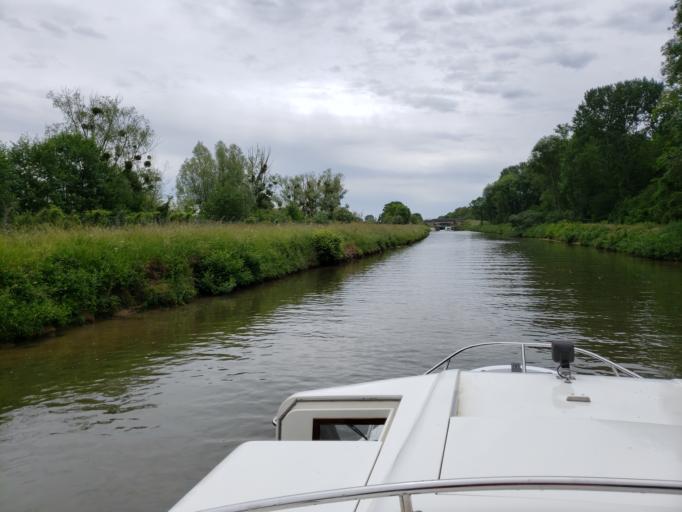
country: FR
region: Bourgogne
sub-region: Departement de l'Yonne
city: Appoigny
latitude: 47.8999
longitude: 3.5354
